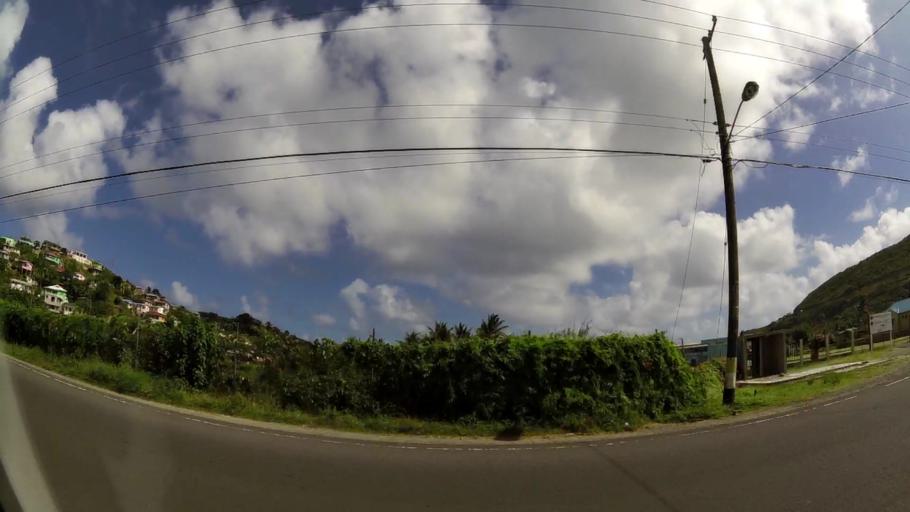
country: LC
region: Dennery Quarter
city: Dennery
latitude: 13.9106
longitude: -60.8943
